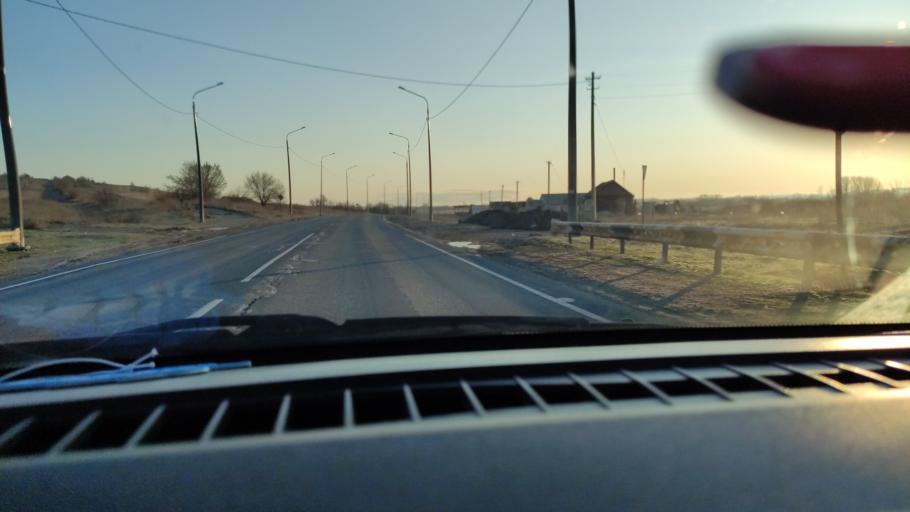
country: RU
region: Saratov
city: Sinodskoye
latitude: 52.0871
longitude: 46.8038
